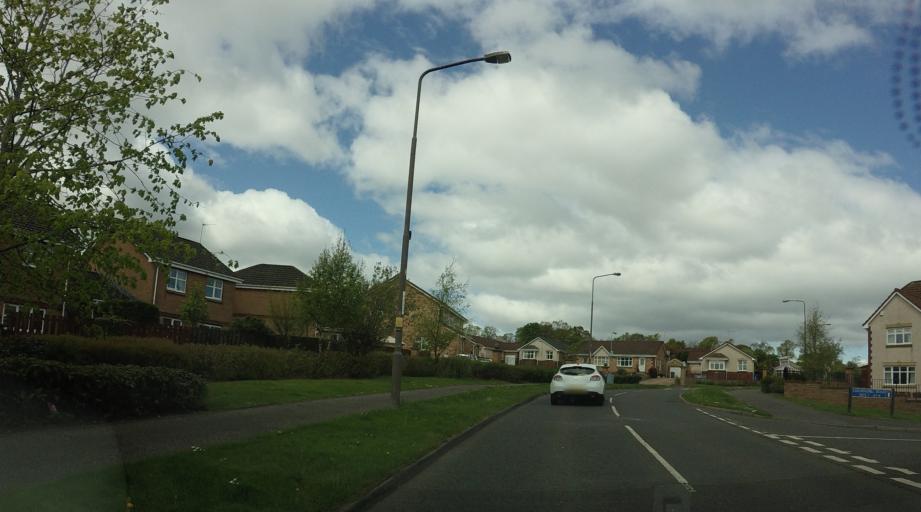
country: GB
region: Scotland
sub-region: West Lothian
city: Broxburn
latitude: 55.9287
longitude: -3.4958
